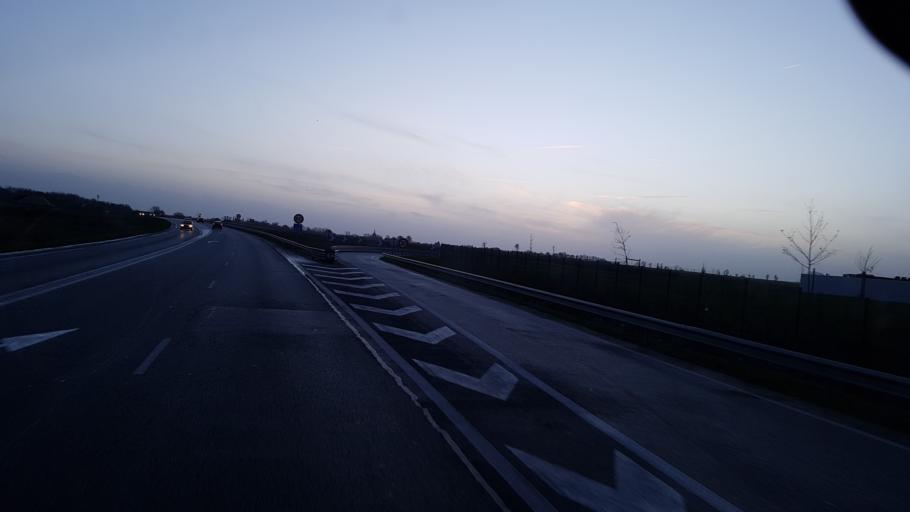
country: FR
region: Nord-Pas-de-Calais
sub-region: Departement du Nord
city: Lauwin-Planque
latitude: 50.3884
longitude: 3.0288
